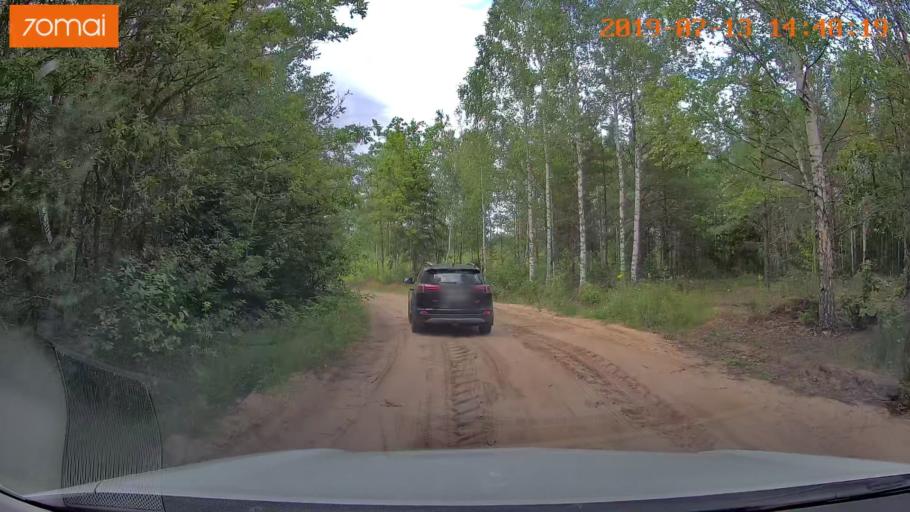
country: BY
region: Mogilev
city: Asipovichy
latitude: 53.2053
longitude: 28.7504
